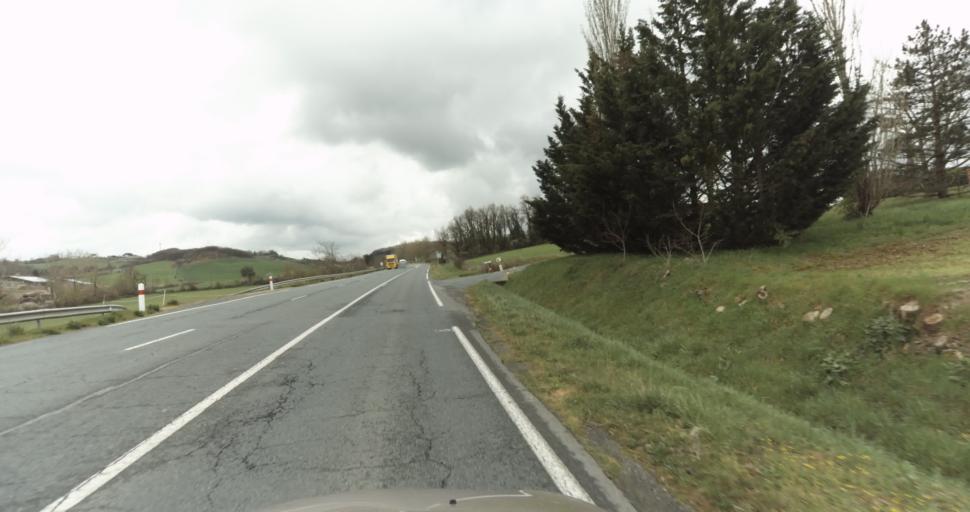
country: FR
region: Midi-Pyrenees
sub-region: Departement du Tarn
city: Puygouzon
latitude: 43.8770
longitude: 2.1771
